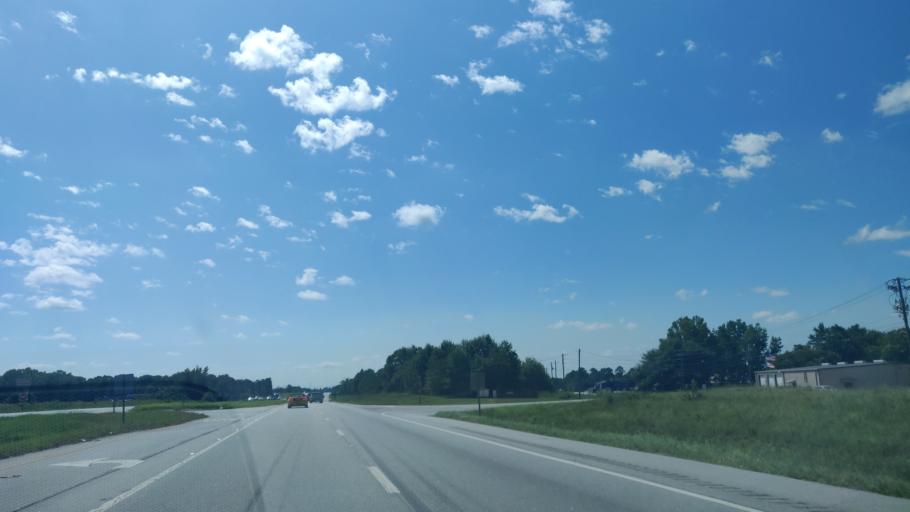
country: US
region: Alabama
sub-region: Lee County
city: Smiths Station
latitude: 32.5637
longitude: -85.1267
